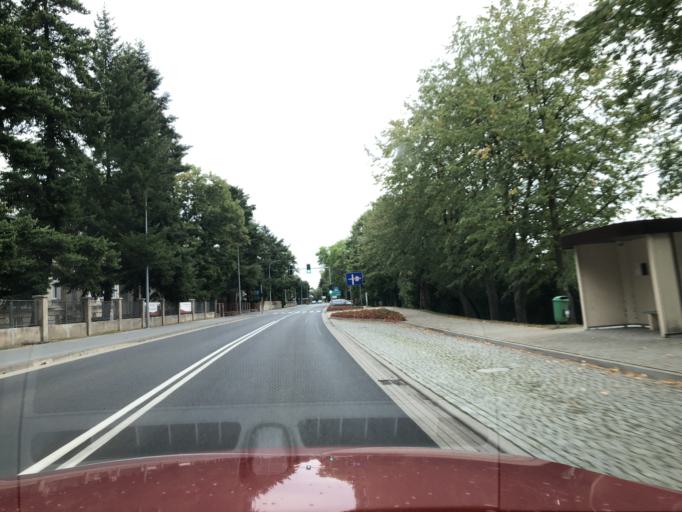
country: PL
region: Greater Poland Voivodeship
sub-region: Powiat szamotulski
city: Pniewy
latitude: 52.5165
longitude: 16.2452
